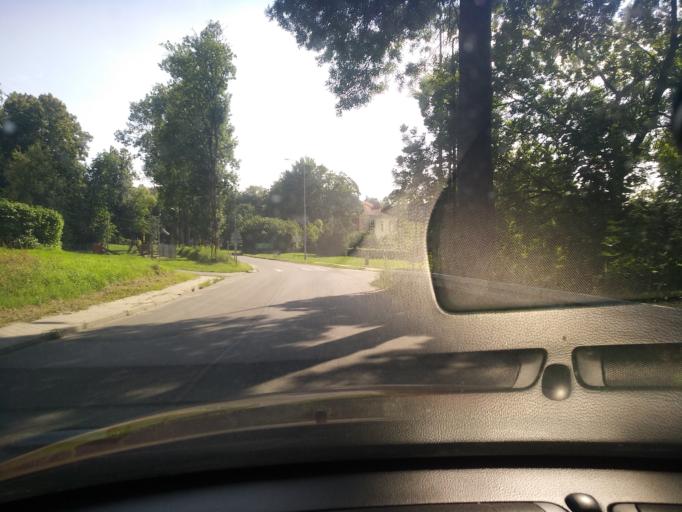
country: PL
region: Lower Silesian Voivodeship
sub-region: Powiat lubanski
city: Lesna
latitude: 51.0250
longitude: 15.2706
